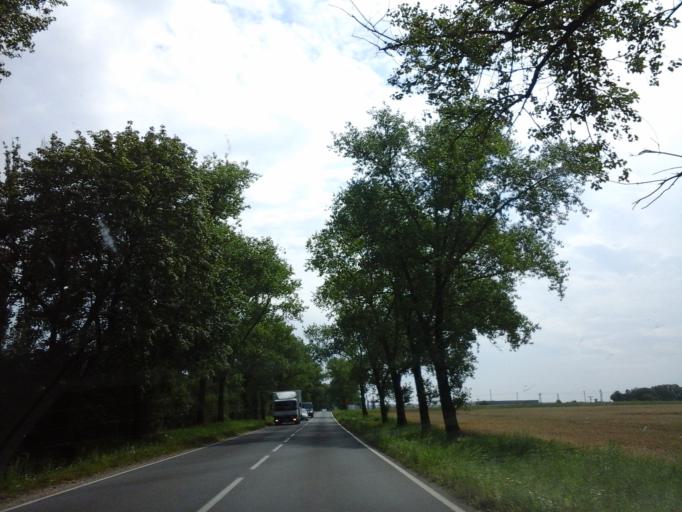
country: PL
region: Lower Silesian Voivodeship
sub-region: Powiat strzelinski
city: Strzelin
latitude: 50.7974
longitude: 17.0641
